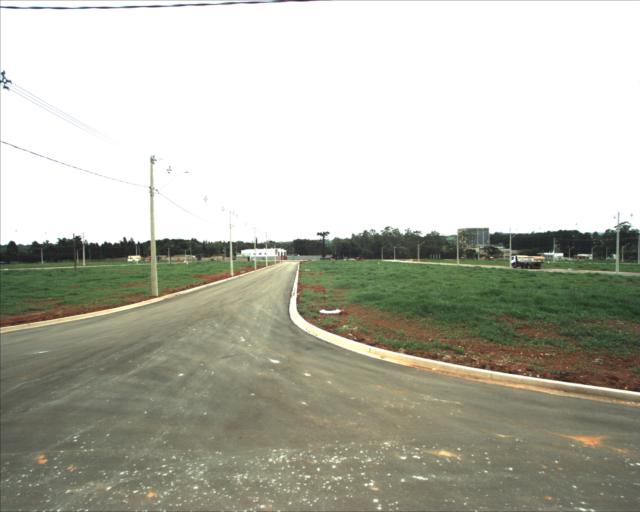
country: BR
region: Sao Paulo
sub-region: Sorocaba
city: Sorocaba
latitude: -23.4180
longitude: -47.4285
